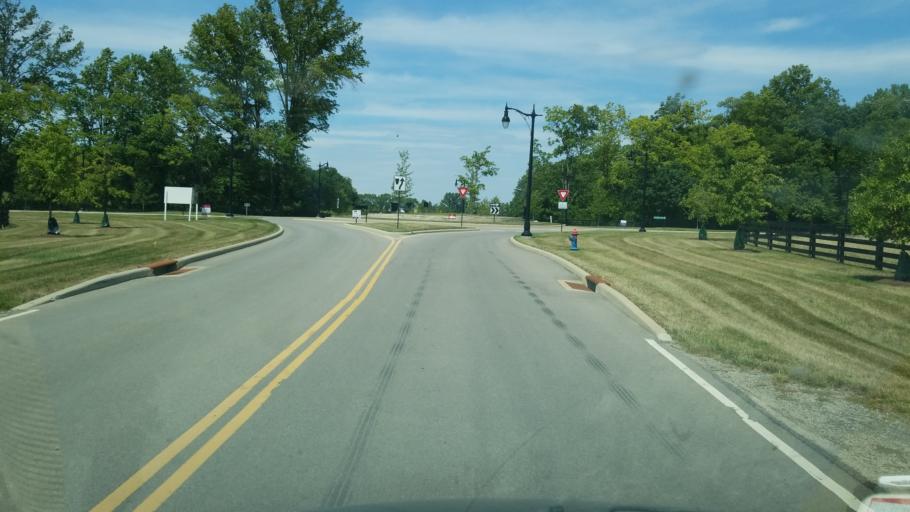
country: US
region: Ohio
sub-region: Union County
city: New California
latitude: 40.1828
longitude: -83.1905
